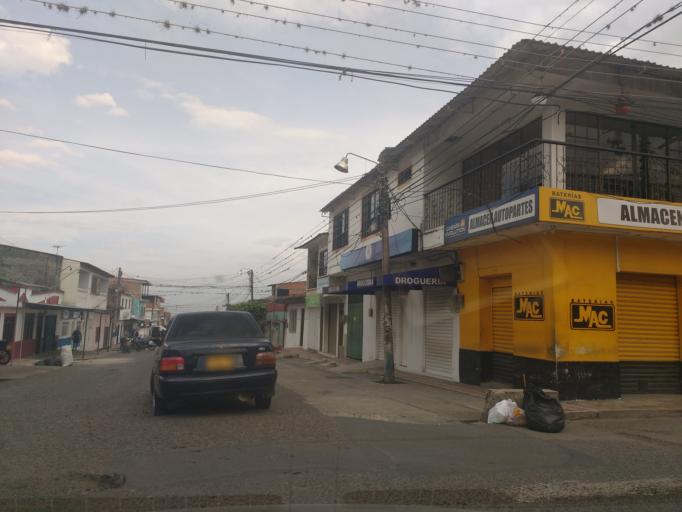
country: CO
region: Cauca
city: Miranda
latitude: 3.2533
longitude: -76.2296
